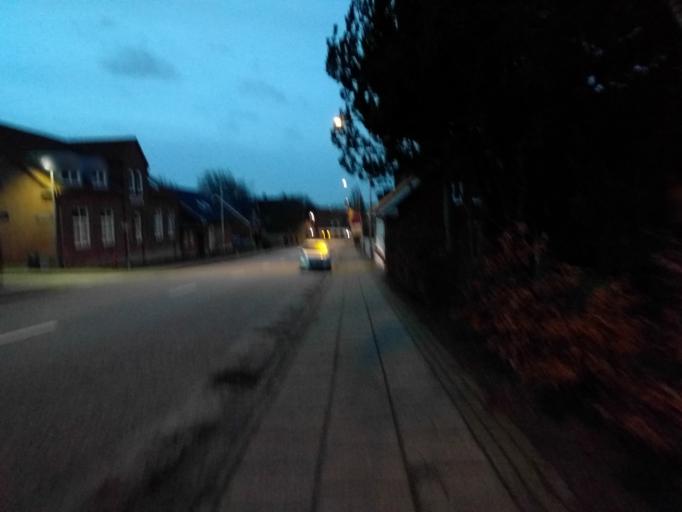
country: DK
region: North Denmark
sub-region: Alborg Kommune
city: Aalborg
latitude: 57.0614
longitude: 9.9235
